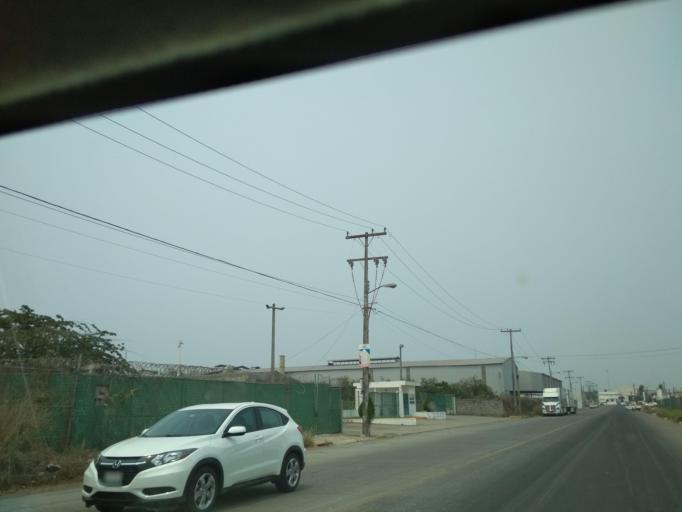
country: MX
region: Veracruz
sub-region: Veracruz
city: Las Amapolas
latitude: 19.1593
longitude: -96.2295
